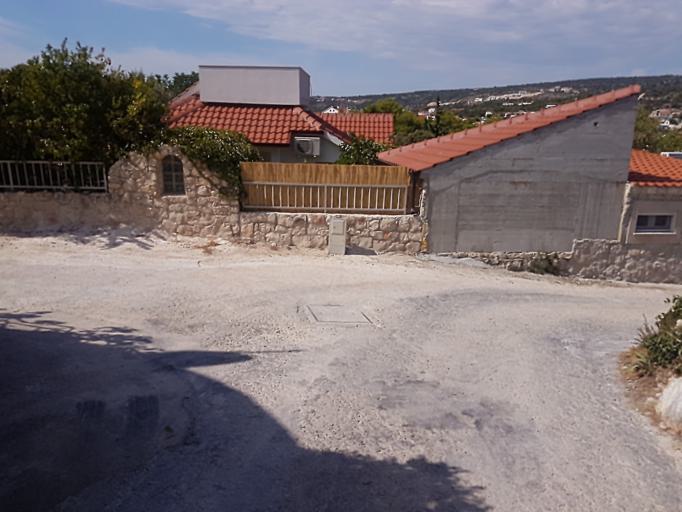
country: HR
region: Sibensko-Kniniska
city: Rogoznica
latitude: 43.4869
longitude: 16.0202
